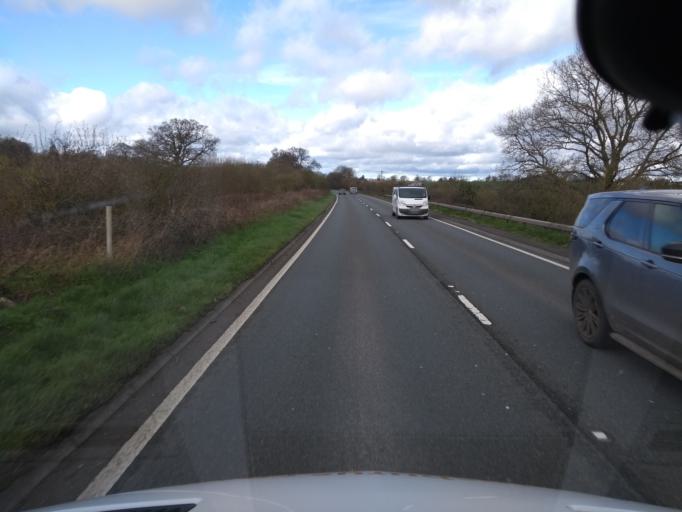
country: GB
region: England
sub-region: Somerset
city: Stoke-sub-Hamdon
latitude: 50.9508
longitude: -2.6988
